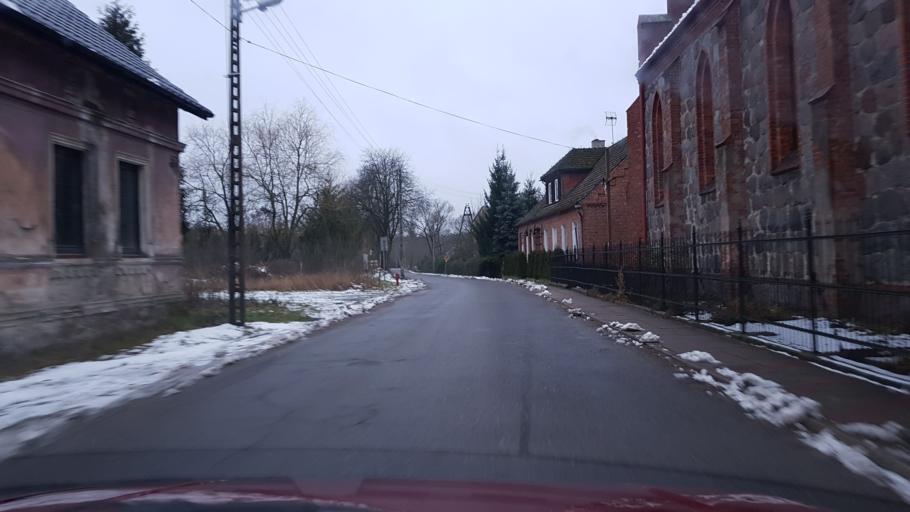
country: PL
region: West Pomeranian Voivodeship
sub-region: Powiat goleniowski
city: Mosty
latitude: 53.4964
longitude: 14.8985
